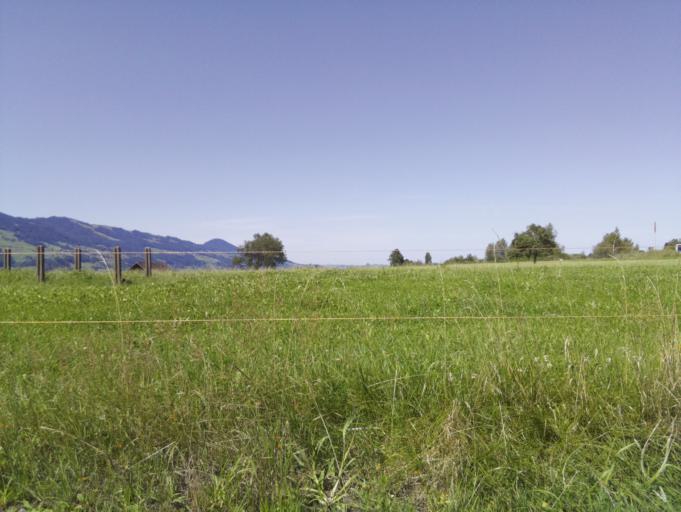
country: CH
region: Schwyz
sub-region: Bezirk March
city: Schubelbach
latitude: 47.1945
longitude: 8.9104
